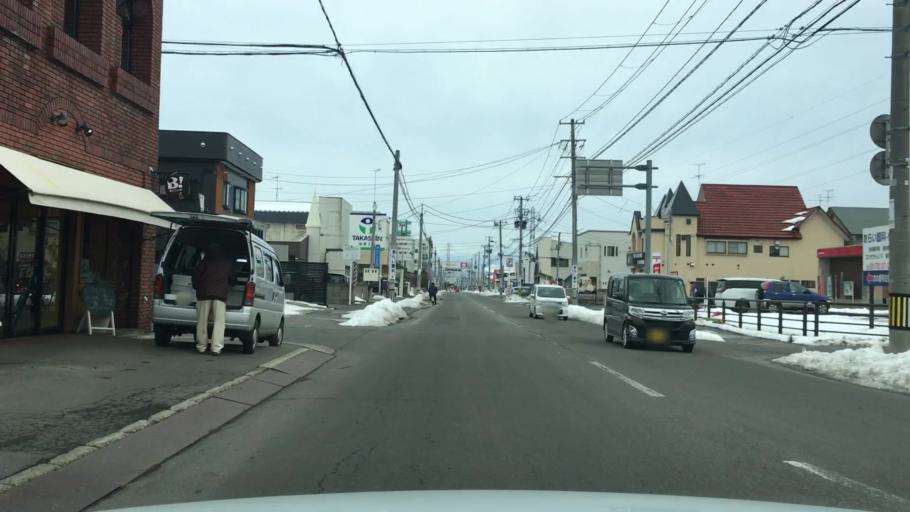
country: JP
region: Aomori
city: Hirosaki
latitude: 40.5993
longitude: 140.4922
